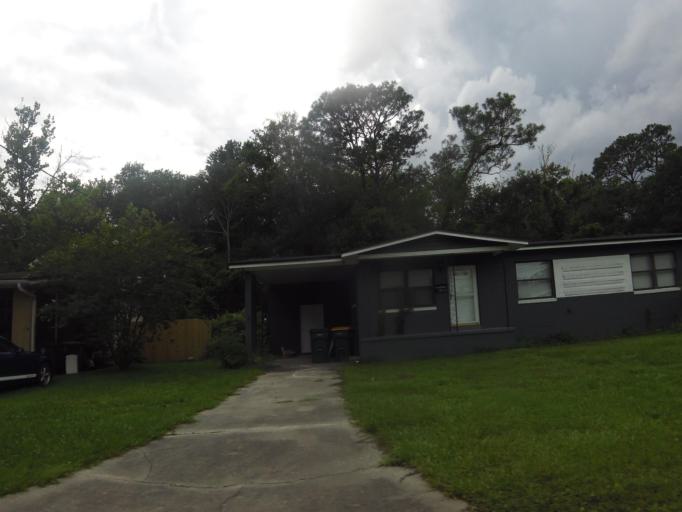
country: US
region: Florida
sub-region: Duval County
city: Jacksonville
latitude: 30.3113
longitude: -81.5373
